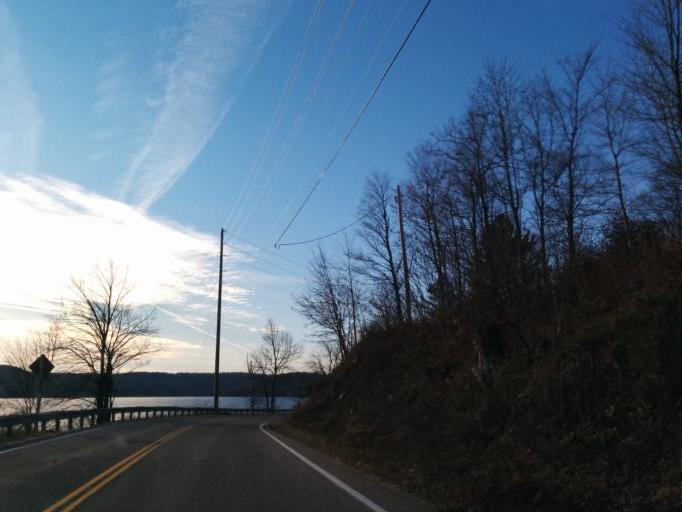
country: CA
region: Ontario
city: Bancroft
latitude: 45.0228
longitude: -78.3688
